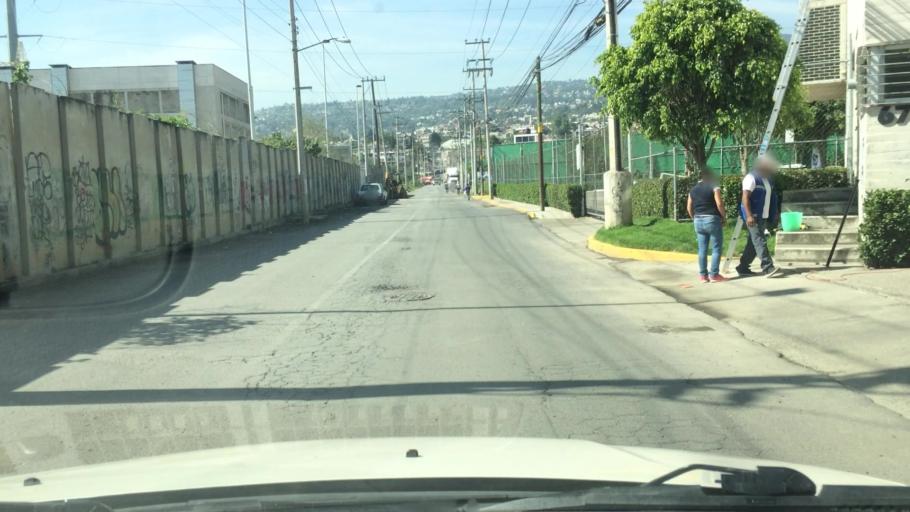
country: MX
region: Mexico City
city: Tlalpan
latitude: 19.2610
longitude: -99.1723
